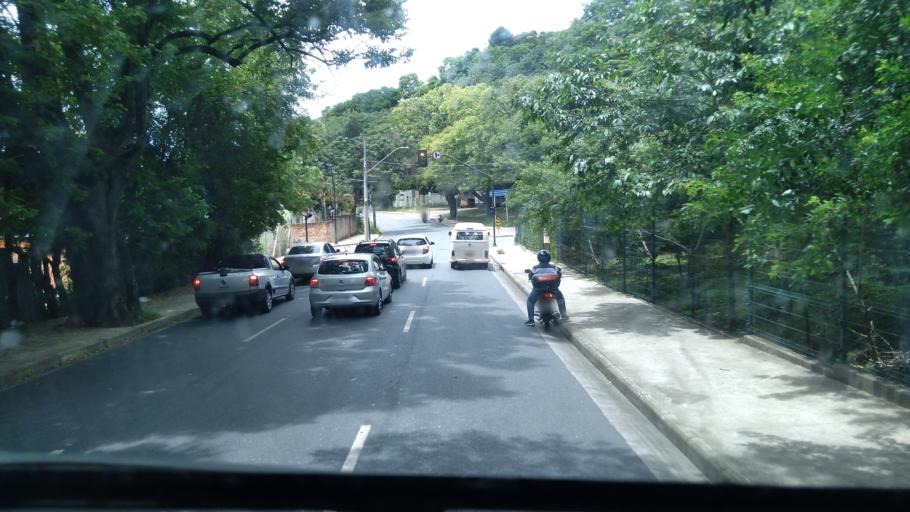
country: BR
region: Minas Gerais
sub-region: Belo Horizonte
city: Belo Horizonte
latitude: -19.8898
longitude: -43.9131
